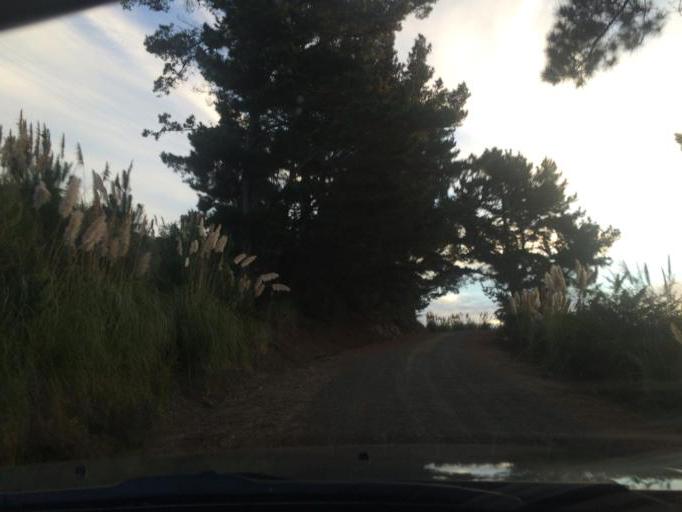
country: NZ
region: Northland
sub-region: Whangarei
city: Maungatapere
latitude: -35.8055
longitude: 174.0428
